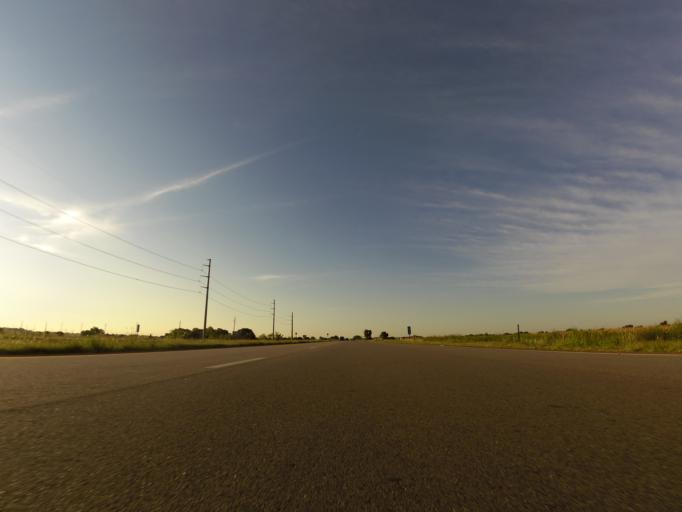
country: US
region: Kansas
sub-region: Sedgwick County
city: Maize
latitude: 37.7763
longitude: -97.4574
